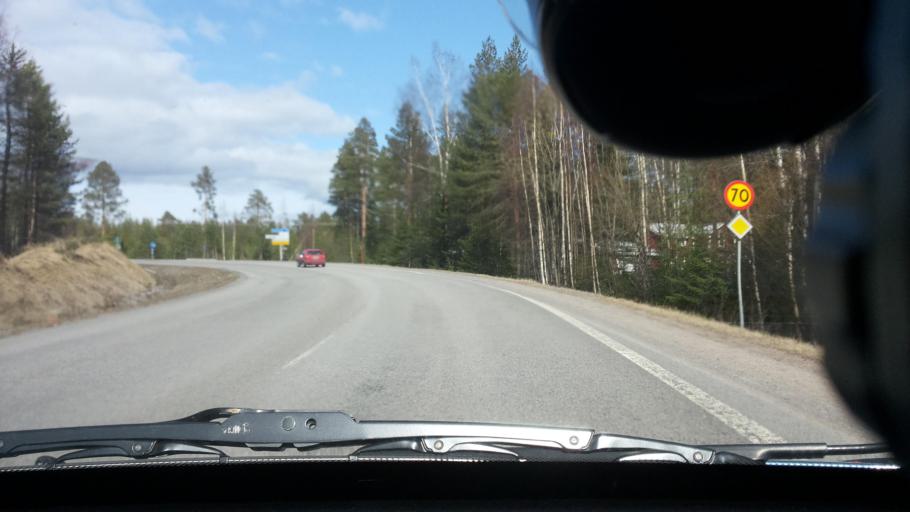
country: SE
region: Norrbotten
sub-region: Lulea Kommun
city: Gammelstad
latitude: 65.5941
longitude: 22.0457
